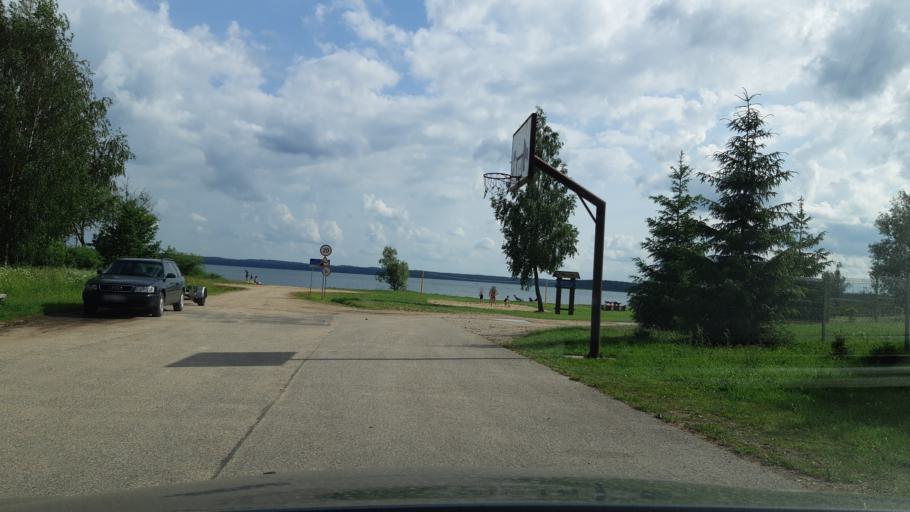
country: LT
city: Kybartai
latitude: 54.4526
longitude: 22.7203
